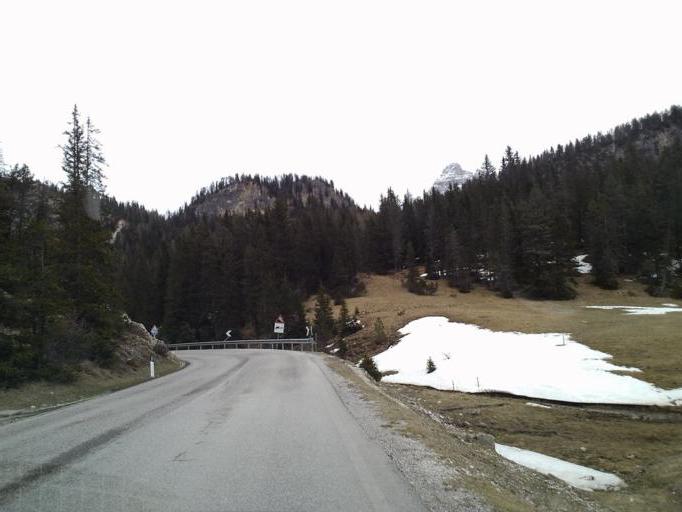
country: IT
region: Veneto
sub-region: Provincia di Belluno
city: Cortina d'Ampezzo
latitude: 46.5961
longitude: 12.2522
